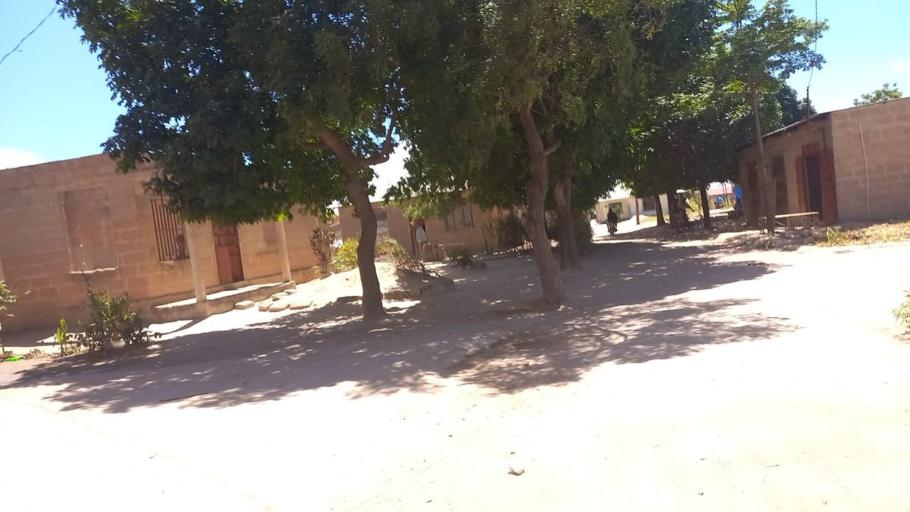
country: TZ
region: Dodoma
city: Dodoma
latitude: -6.1310
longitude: 35.7339
